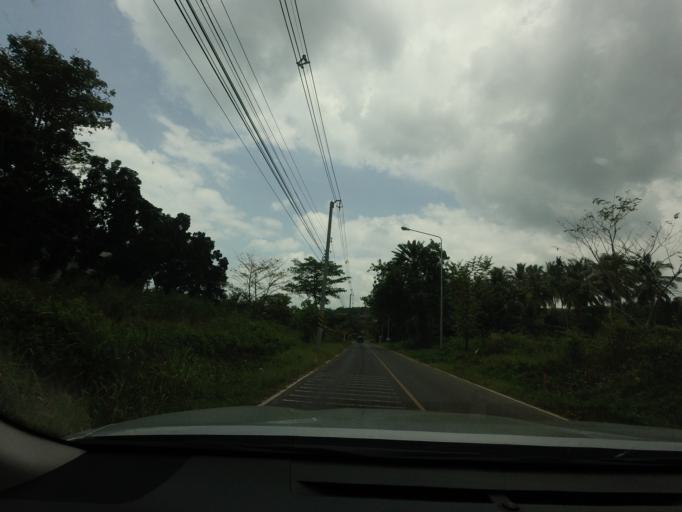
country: TH
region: Phangnga
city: Ban Ao Nang
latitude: 8.0741
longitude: 98.7459
